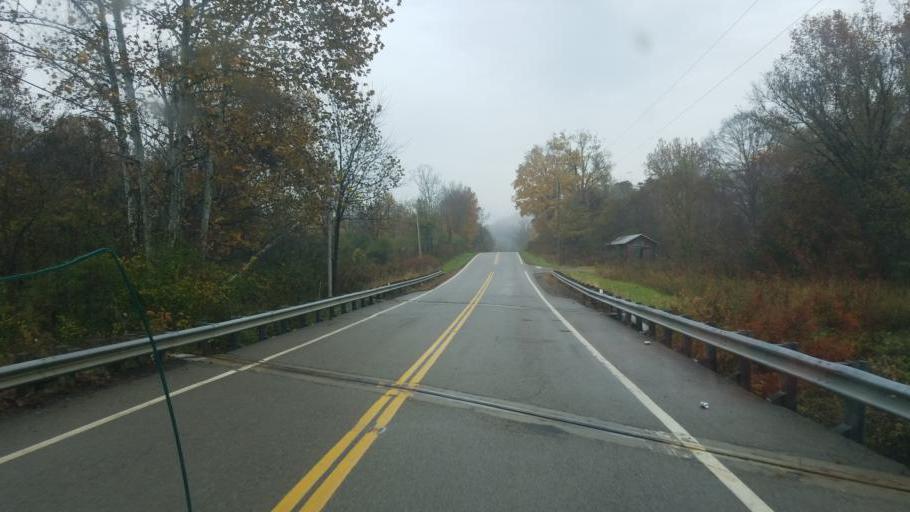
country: US
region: Ohio
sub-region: Athens County
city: Glouster
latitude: 39.4464
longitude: -81.8988
